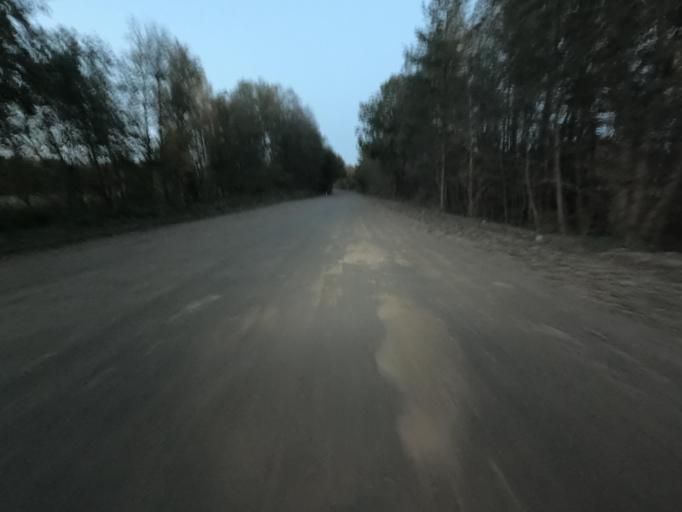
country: RU
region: Leningrad
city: Lyuban'
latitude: 59.1861
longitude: 31.2465
